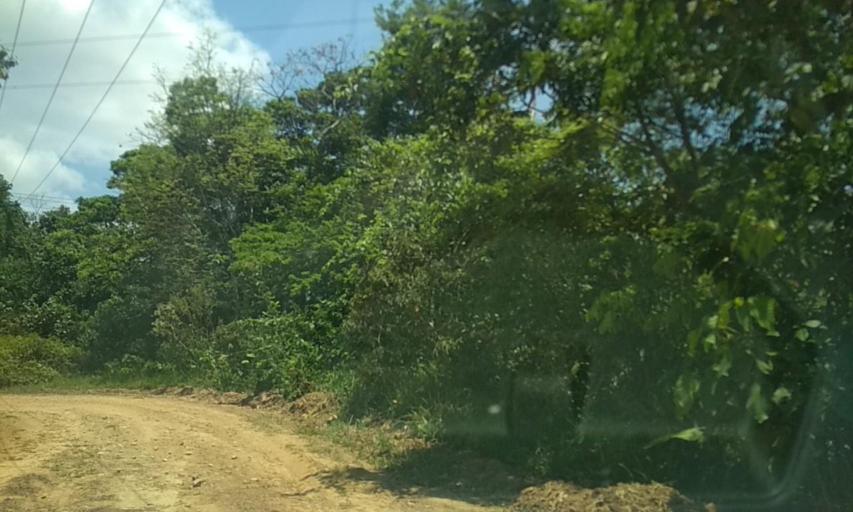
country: MX
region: Chiapas
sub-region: Tecpatan
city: Raudales Malpaso
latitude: 17.3969
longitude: -93.7473
